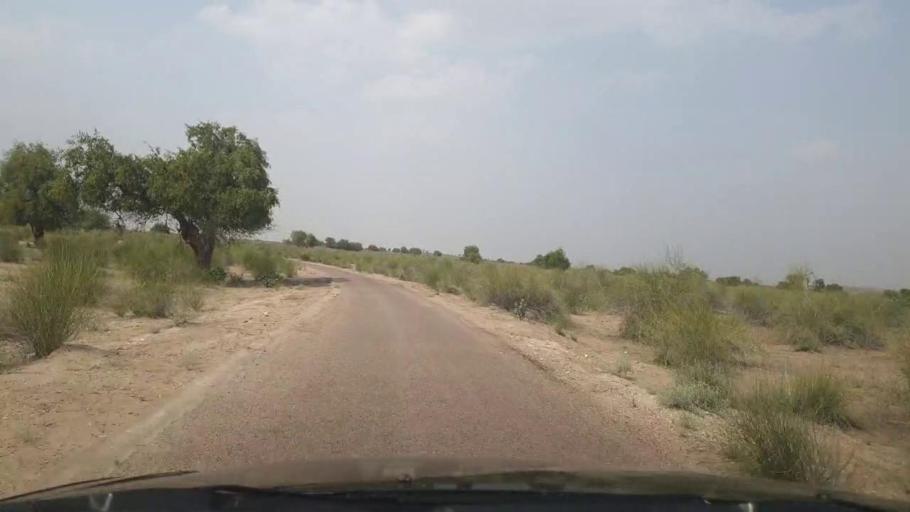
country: PK
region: Sindh
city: Islamkot
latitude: 24.9366
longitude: 70.5729
